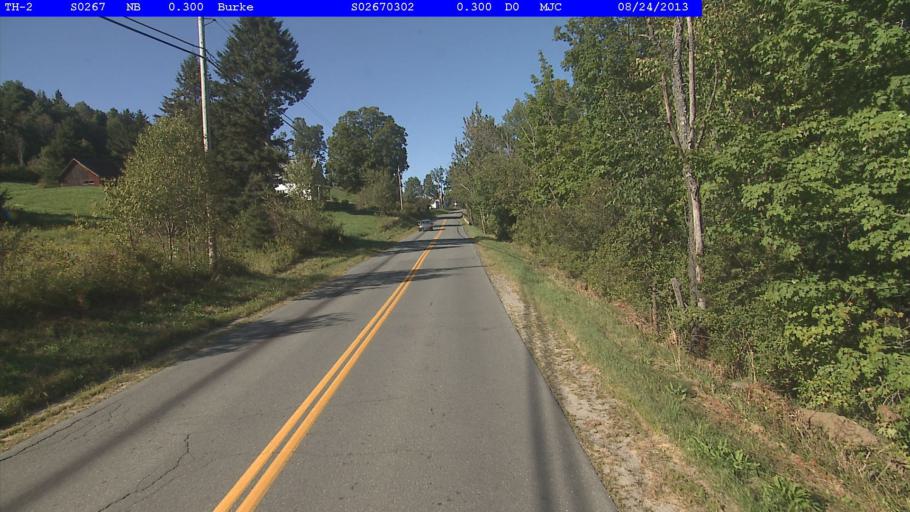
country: US
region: Vermont
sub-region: Caledonia County
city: Lyndonville
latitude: 44.5915
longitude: -71.9452
